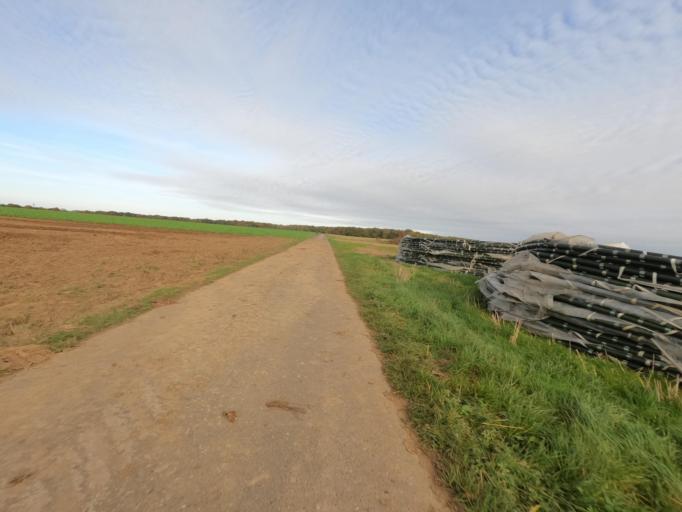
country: DE
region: North Rhine-Westphalia
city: Erkelenz
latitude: 51.0431
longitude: 6.3297
